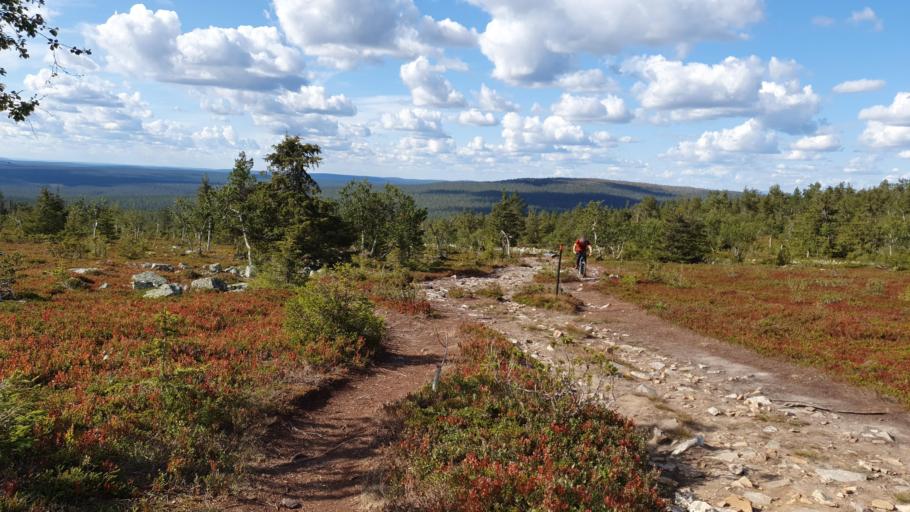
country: FI
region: Lapland
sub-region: Tunturi-Lappi
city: Kolari
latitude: 67.6141
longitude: 24.2600
